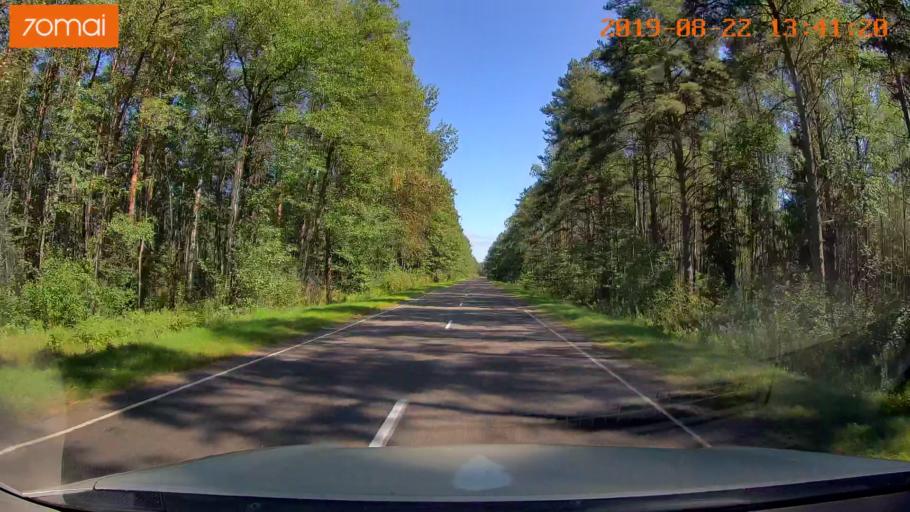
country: BY
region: Minsk
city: Staryya Darohi
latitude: 53.2385
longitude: 28.3939
